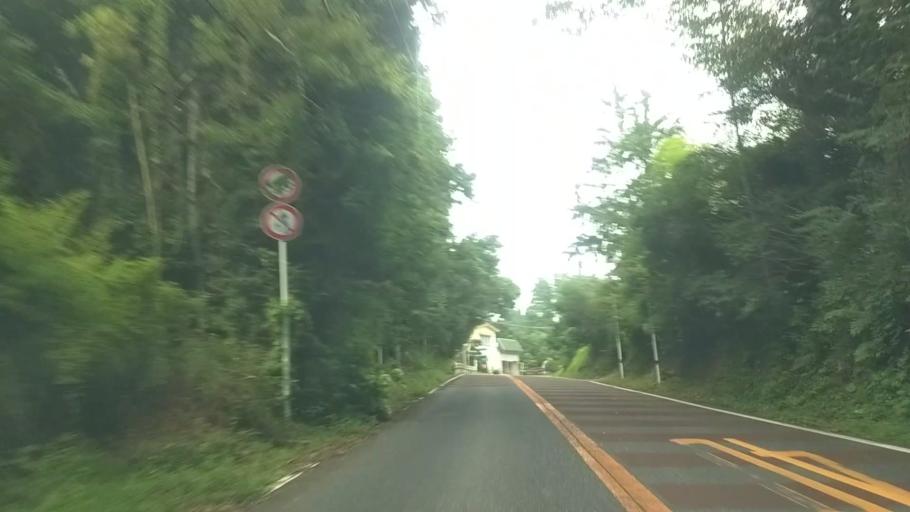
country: JP
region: Chiba
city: Kawaguchi
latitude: 35.2080
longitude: 140.0691
